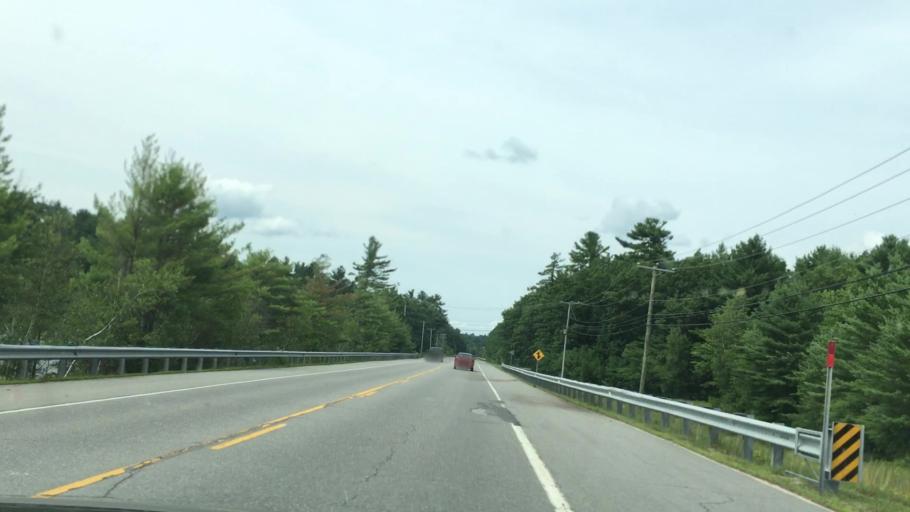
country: US
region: New Hampshire
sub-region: Cheshire County
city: Rindge
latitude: 42.7759
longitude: -72.0330
